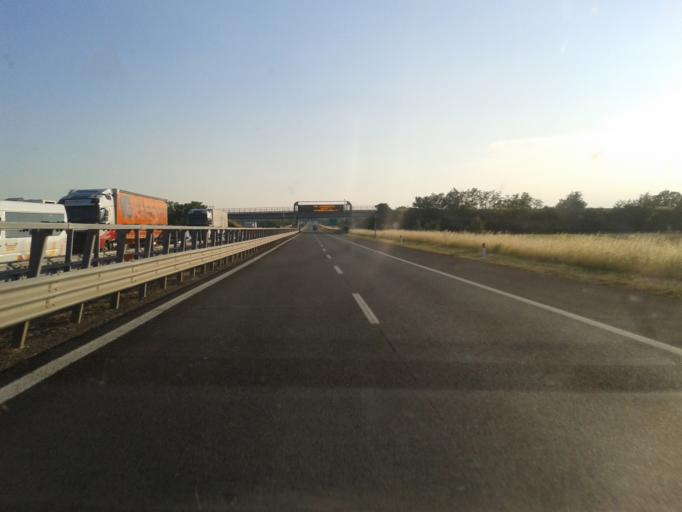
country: IT
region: Piedmont
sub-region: Provincia di Alessandria
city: Predosa
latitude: 44.7686
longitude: 8.6594
